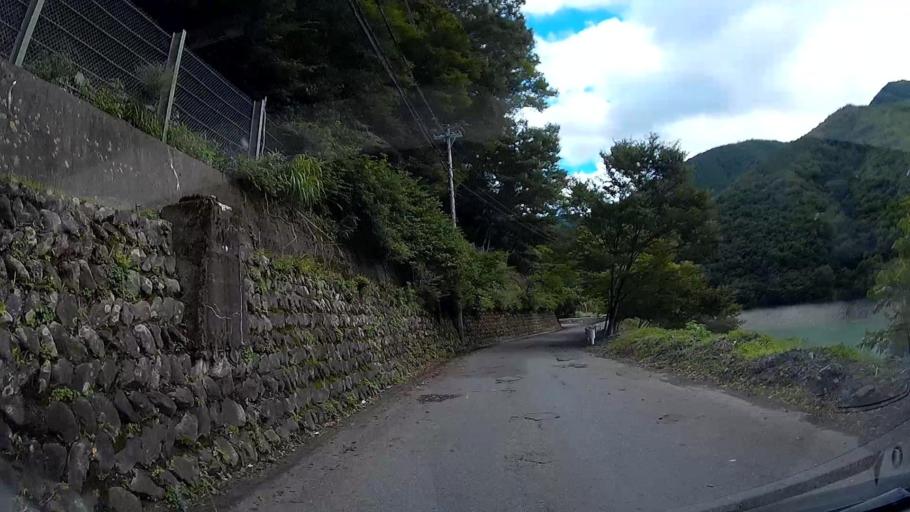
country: JP
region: Shizuoka
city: Shizuoka-shi
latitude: 35.3250
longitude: 138.1828
